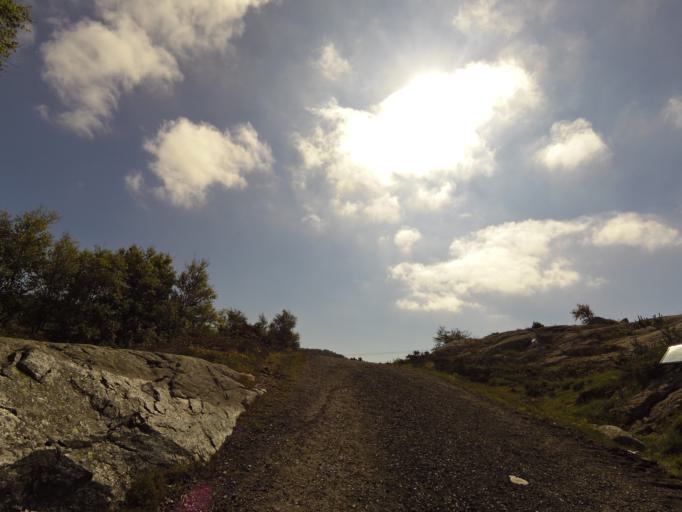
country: NO
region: Rogaland
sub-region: Ha
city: Vigrestad
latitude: 58.5144
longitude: 5.8306
